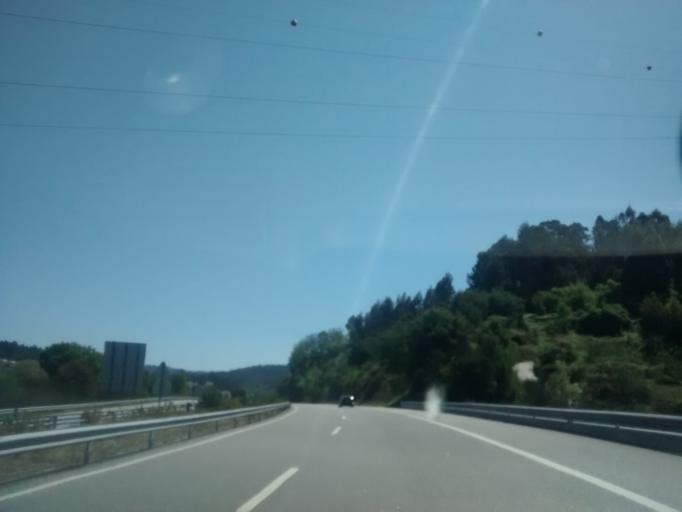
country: PT
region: Braga
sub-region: Guimaraes
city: Candoso
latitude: 41.4216
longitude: -8.3298
